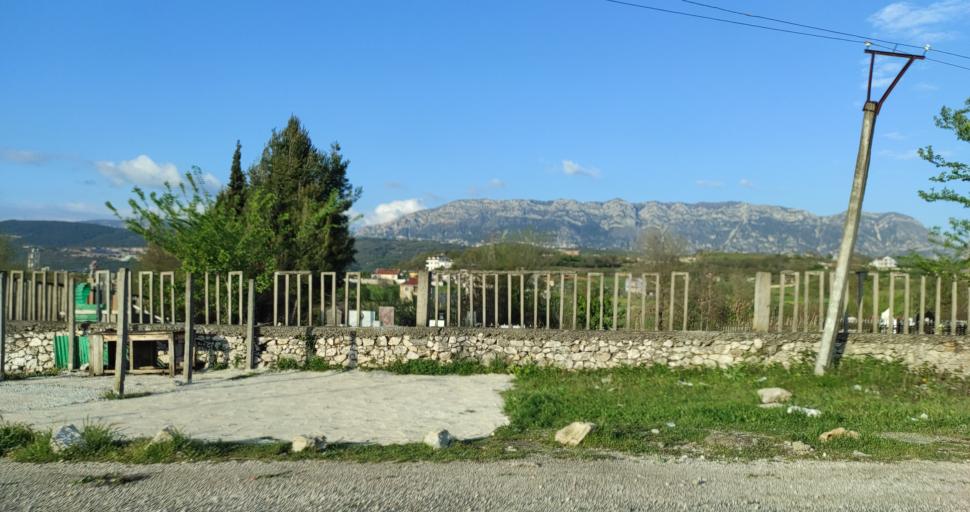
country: AL
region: Durres
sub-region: Rrethi i Krujes
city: Fushe-Kruje
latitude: 41.4835
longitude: 19.7335
